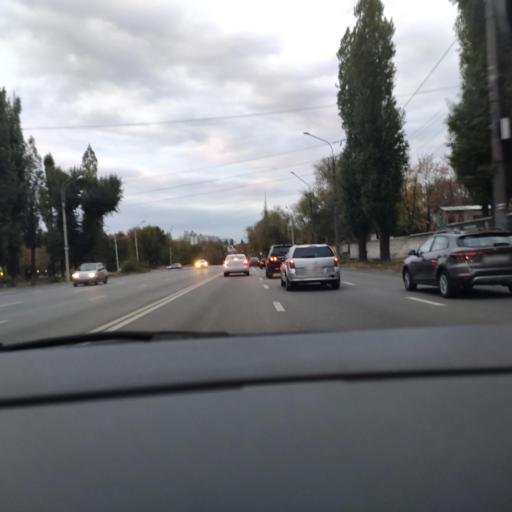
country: RU
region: Voronezj
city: Voronezh
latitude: 51.6888
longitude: 39.1653
